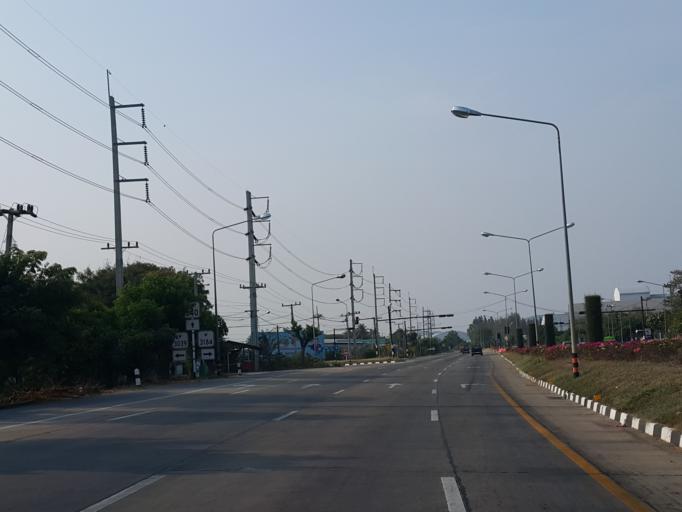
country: TH
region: Chai Nat
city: Hankha
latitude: 14.9420
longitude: 100.0815
